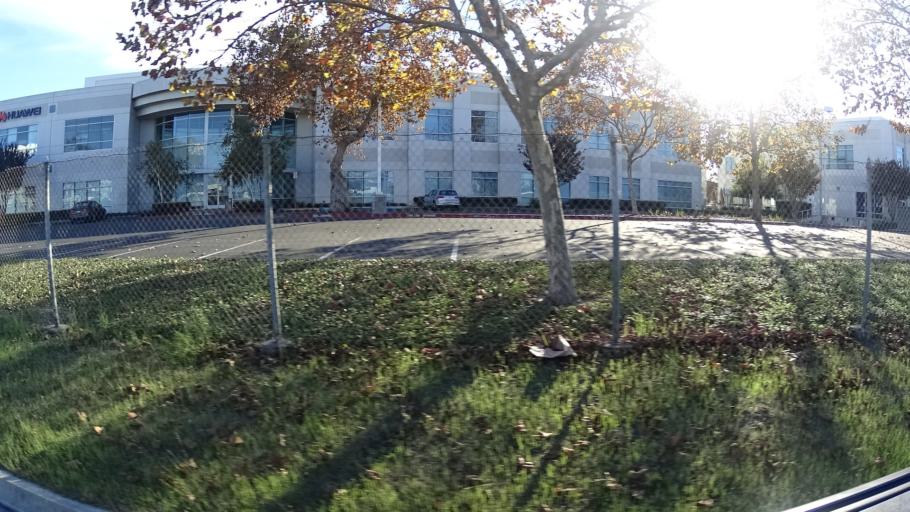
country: US
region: California
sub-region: Santa Clara County
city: Santa Clara
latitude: 37.3739
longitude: -121.9642
